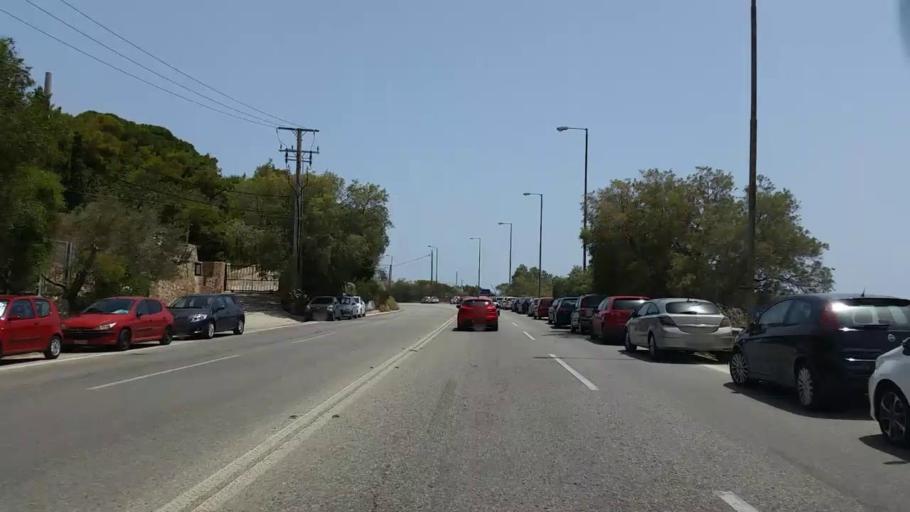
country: GR
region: Attica
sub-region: Nomarchia Anatolikis Attikis
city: Saronida
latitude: 37.7222
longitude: 23.9091
